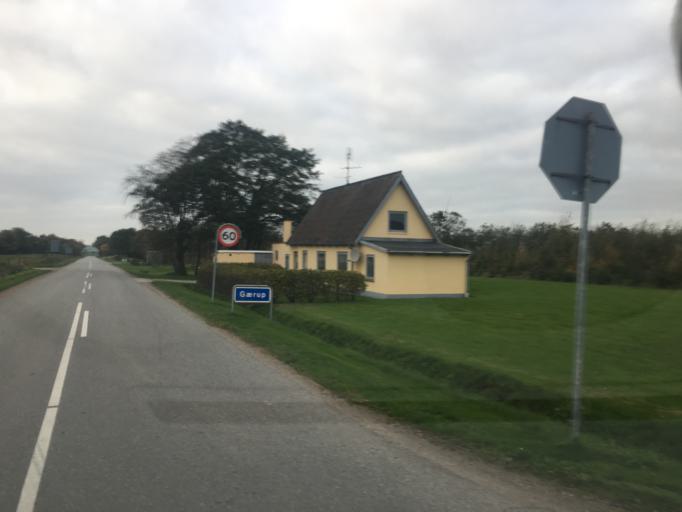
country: DE
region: Schleswig-Holstein
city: Aventoft
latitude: 54.9875
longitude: 8.7676
